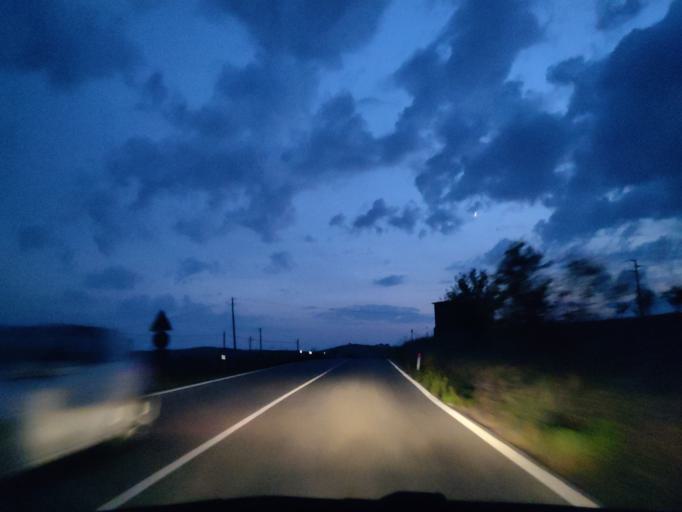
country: IT
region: Latium
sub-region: Provincia di Viterbo
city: Tarquinia
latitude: 42.2552
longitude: 11.8163
